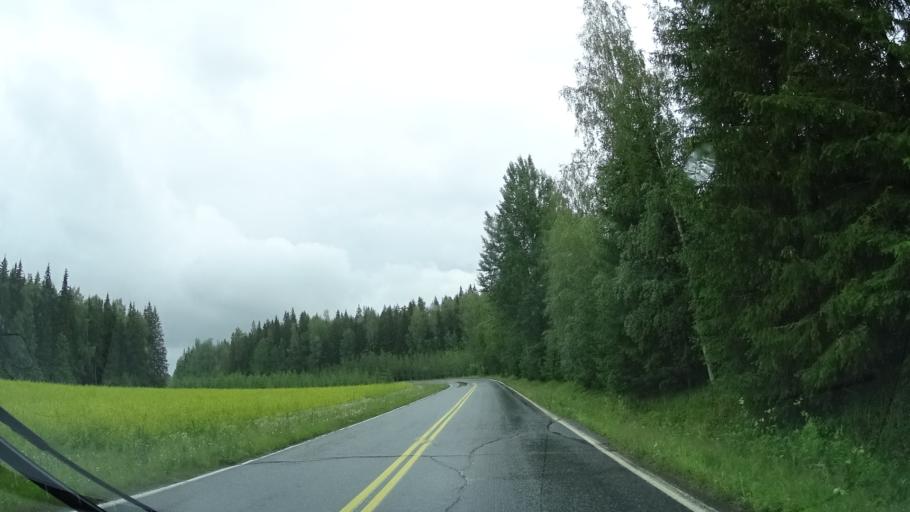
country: FI
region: Haeme
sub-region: Forssa
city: Humppila
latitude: 60.9908
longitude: 23.2563
